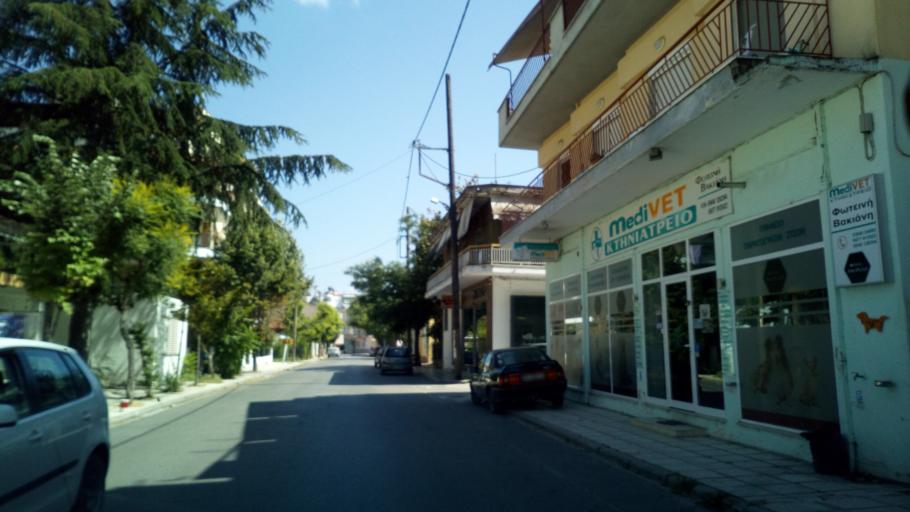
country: GR
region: Central Macedonia
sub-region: Nomos Thessalonikis
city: Lagkadas
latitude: 40.7507
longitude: 23.0686
